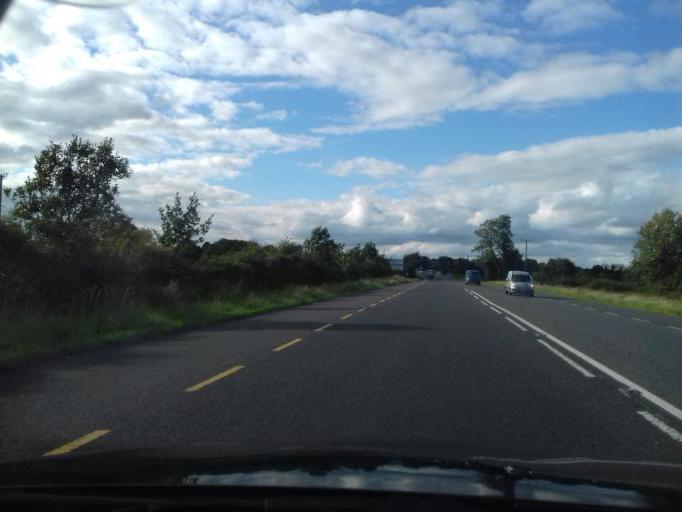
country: IE
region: Leinster
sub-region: Uibh Fhaili
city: Tullamore
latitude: 53.3075
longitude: -7.4958
